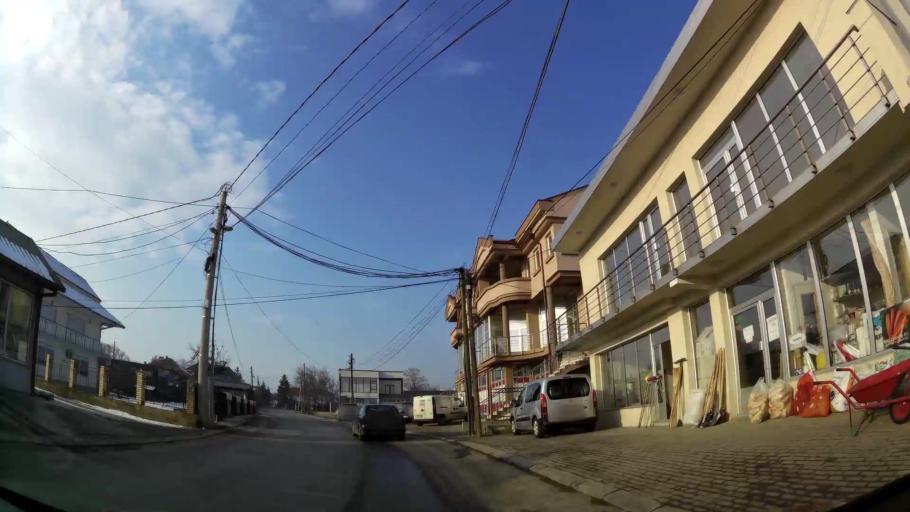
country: MK
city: Creshevo
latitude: 42.0260
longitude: 21.5150
